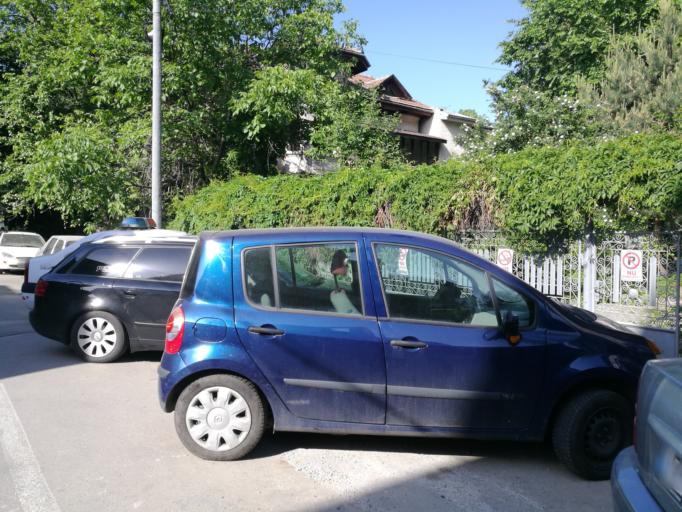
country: RO
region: Bucuresti
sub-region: Municipiul Bucuresti
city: Bucuresti
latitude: 44.4336
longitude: 26.0703
